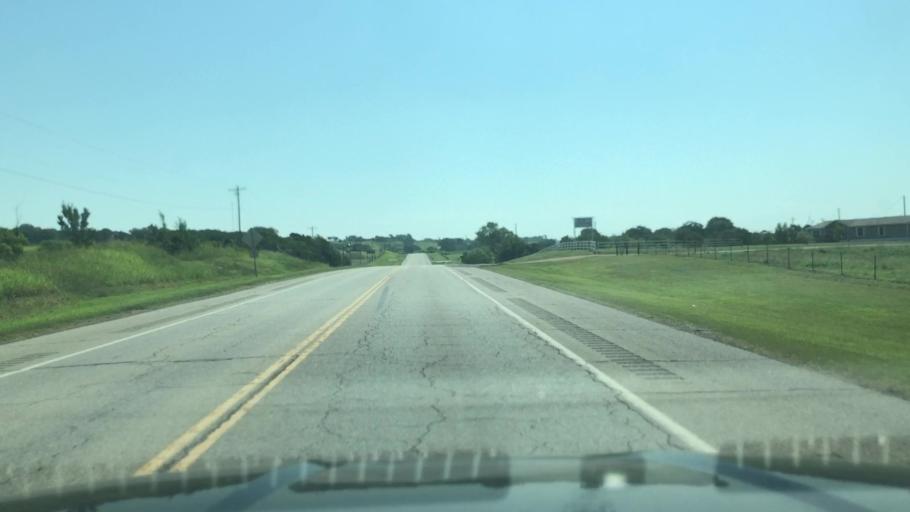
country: US
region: Oklahoma
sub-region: Creek County
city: Drumright
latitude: 35.9884
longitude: -96.5604
